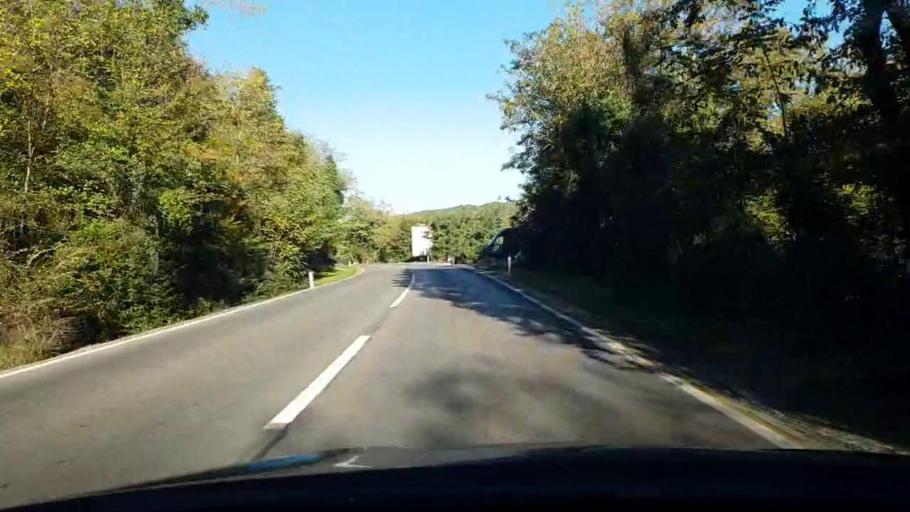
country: ME
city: Igalo
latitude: 42.4782
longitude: 18.4615
